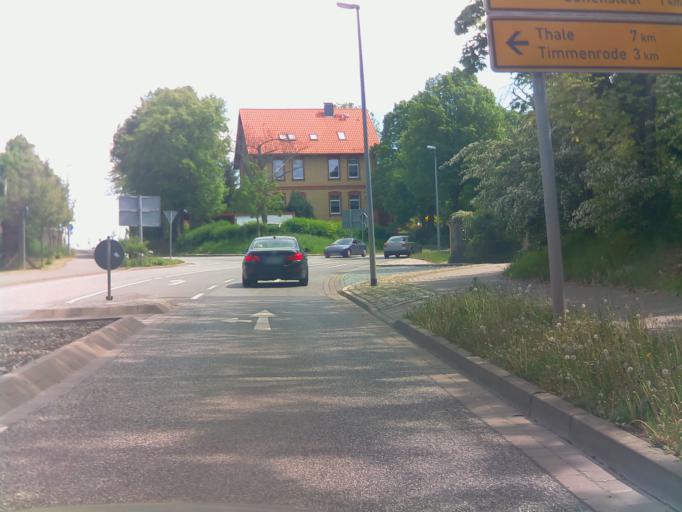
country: DE
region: Saxony-Anhalt
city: Blankenburg
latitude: 51.7845
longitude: 10.9662
